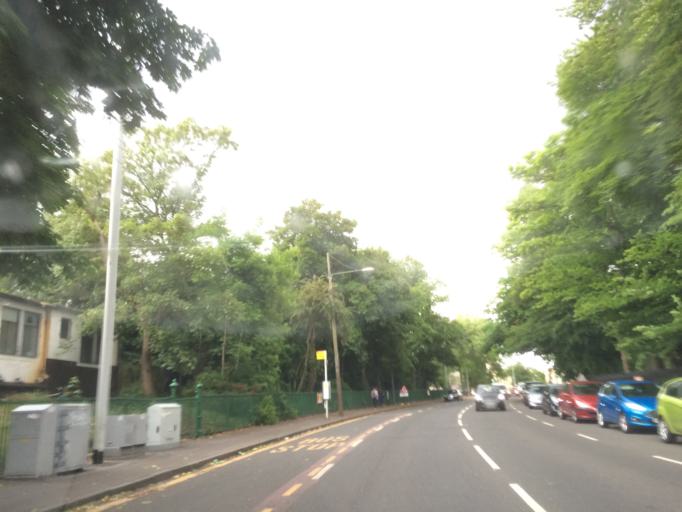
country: GB
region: Scotland
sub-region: Glasgow City
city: Glasgow
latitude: 55.8314
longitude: -4.2631
